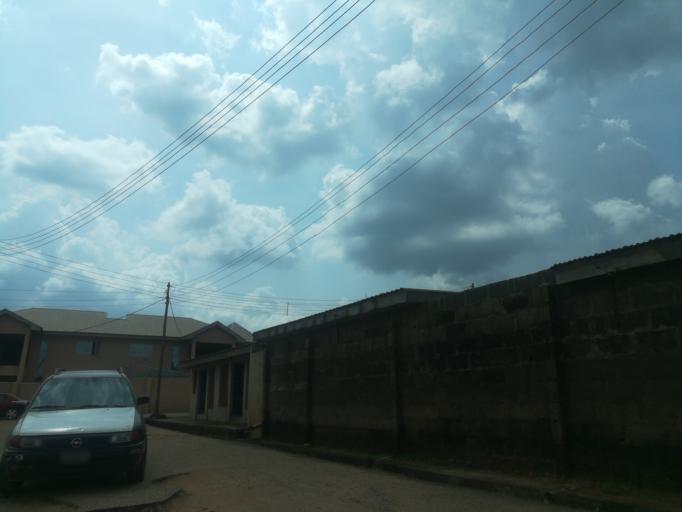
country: NG
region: Oyo
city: Ibadan
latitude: 7.4364
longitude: 3.9354
